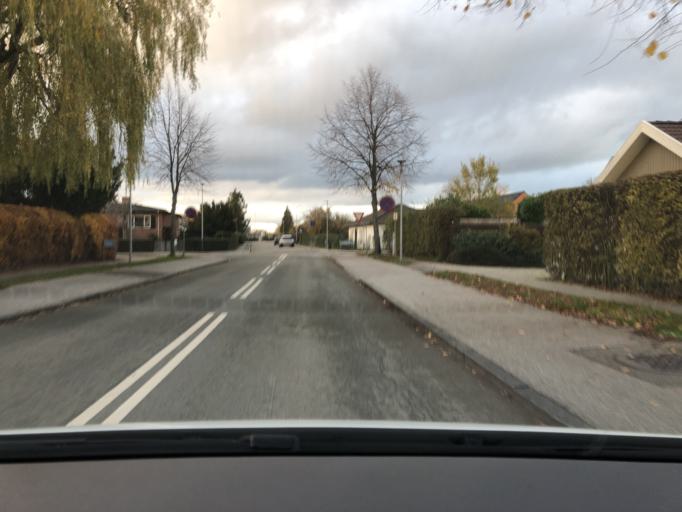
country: DK
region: Capital Region
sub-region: Tarnby Kommune
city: Tarnby
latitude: 55.6213
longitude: 12.5975
